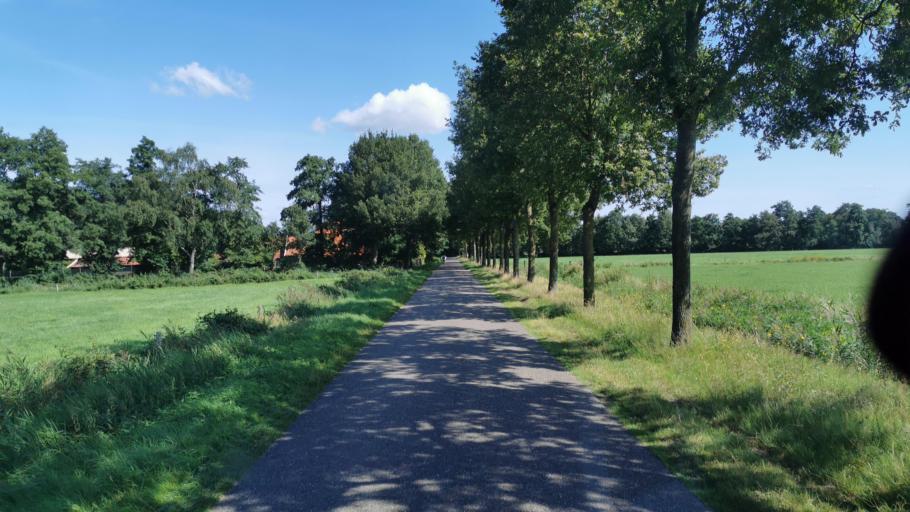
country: DE
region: North Rhine-Westphalia
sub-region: Regierungsbezirk Munster
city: Gronau
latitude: 52.1995
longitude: 6.9623
